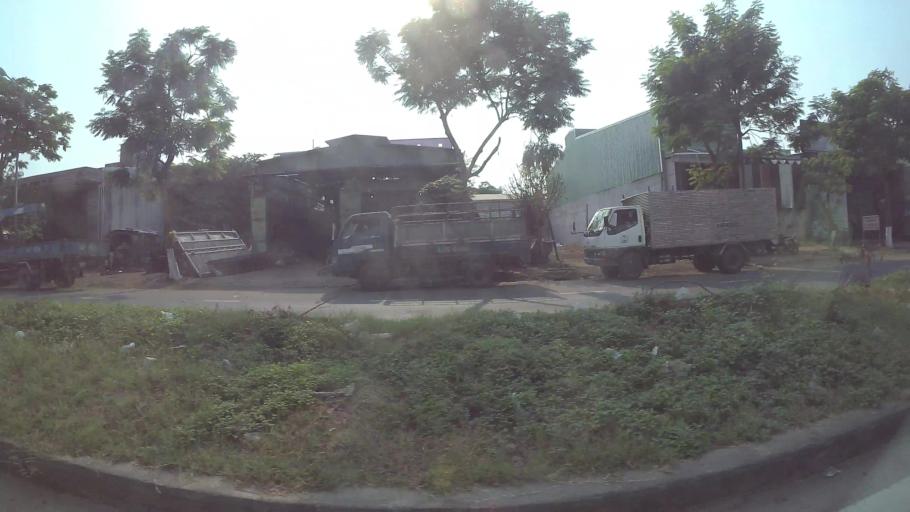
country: VN
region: Da Nang
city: Thanh Khe
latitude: 16.0522
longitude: 108.1738
